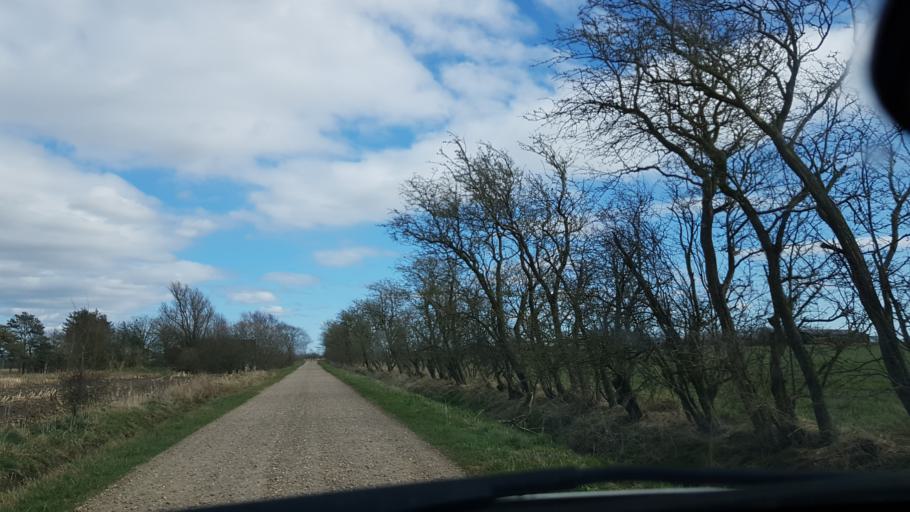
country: DK
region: South Denmark
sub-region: Esbjerg Kommune
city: Ribe
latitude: 55.2854
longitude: 8.8034
